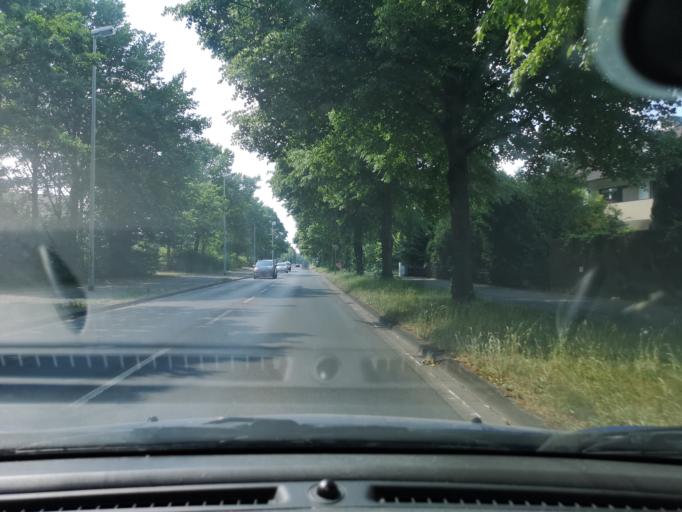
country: DE
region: Lower Saxony
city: Langenhagen
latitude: 52.4180
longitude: 9.7688
